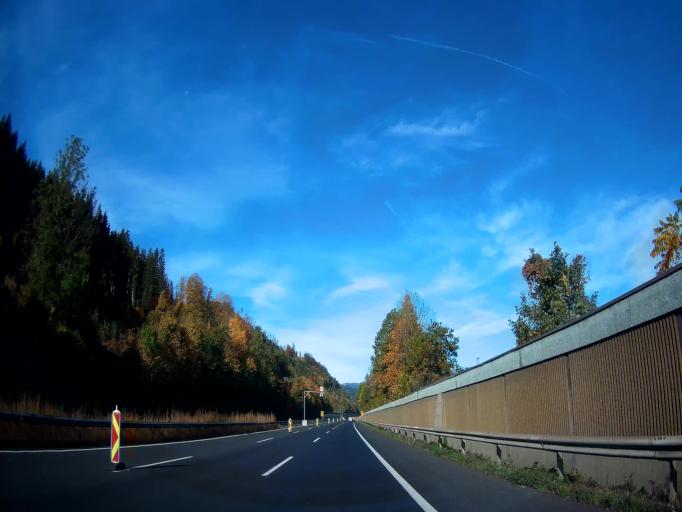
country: AT
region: Styria
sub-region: Politischer Bezirk Graz-Umgebung
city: Ubelbach
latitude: 47.2185
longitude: 15.2473
